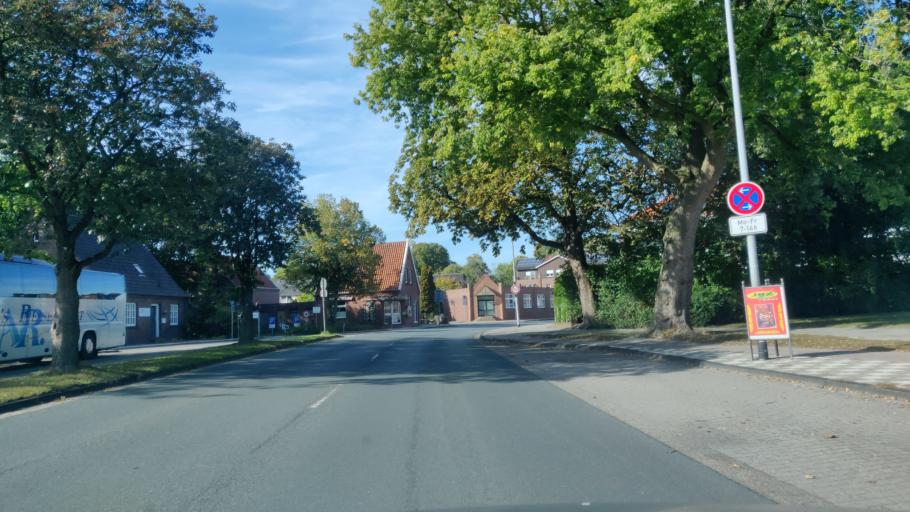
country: DE
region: Lower Saxony
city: Leer
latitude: 53.2272
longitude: 7.4424
